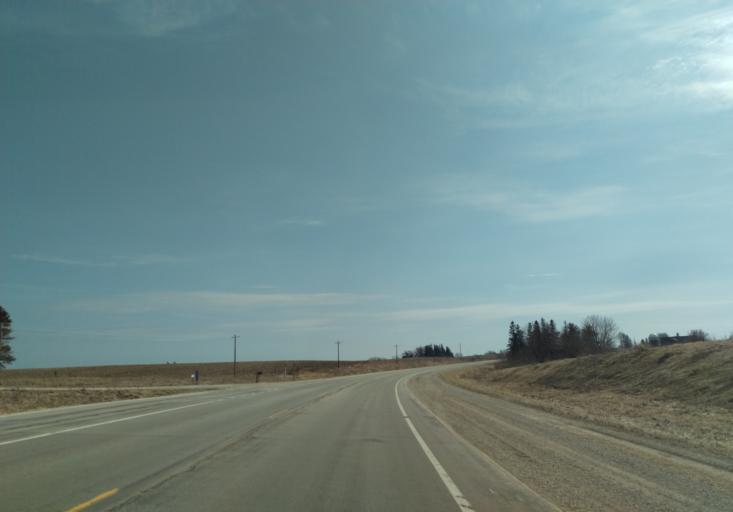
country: US
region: Iowa
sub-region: Winneshiek County
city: Decorah
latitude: 43.4502
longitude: -91.8642
